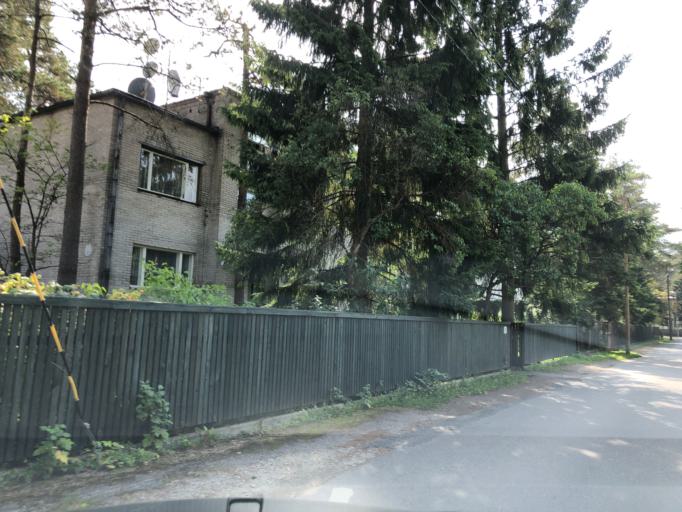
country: EE
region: Harju
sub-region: Tallinna linn
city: Tallinn
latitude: 59.3808
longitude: 24.6944
